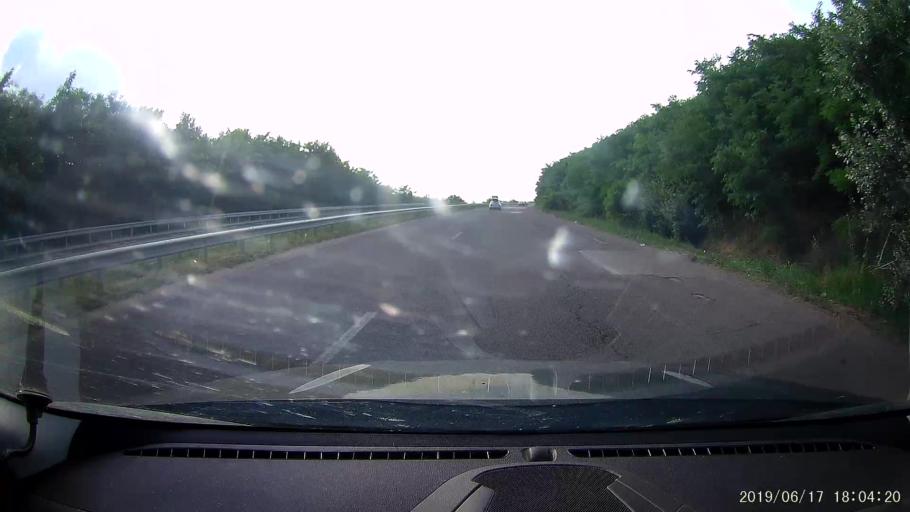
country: BG
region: Khaskovo
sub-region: Obshtina Svilengrad
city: Svilengrad
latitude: 41.7846
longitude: 26.2003
